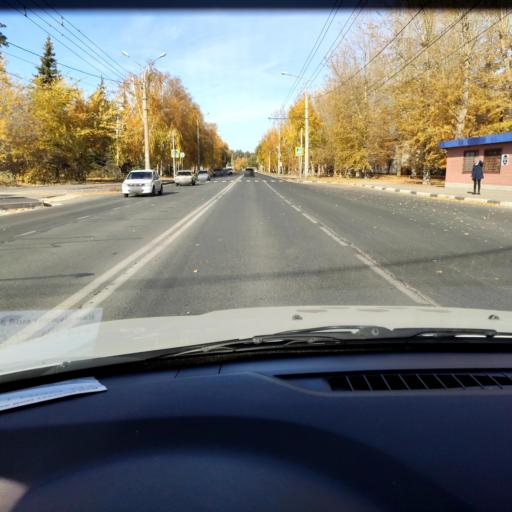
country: RU
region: Samara
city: Tol'yatti
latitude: 53.5022
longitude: 49.3902
